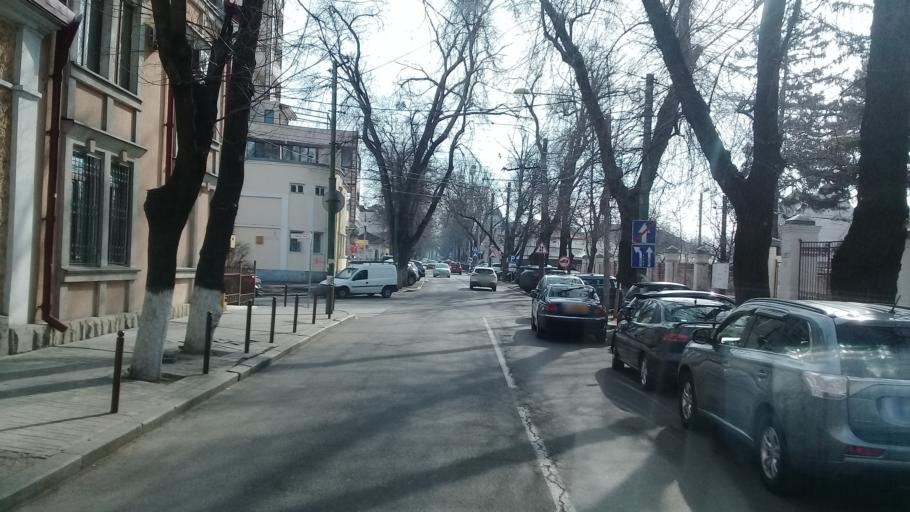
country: MD
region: Chisinau
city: Chisinau
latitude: 47.0231
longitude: 28.8178
